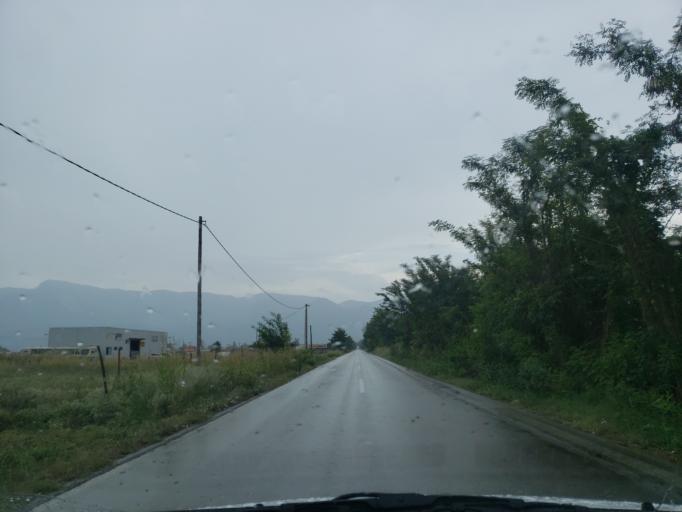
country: GR
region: Central Greece
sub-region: Nomos Fthiotidos
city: Anthili
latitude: 38.8385
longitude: 22.4411
